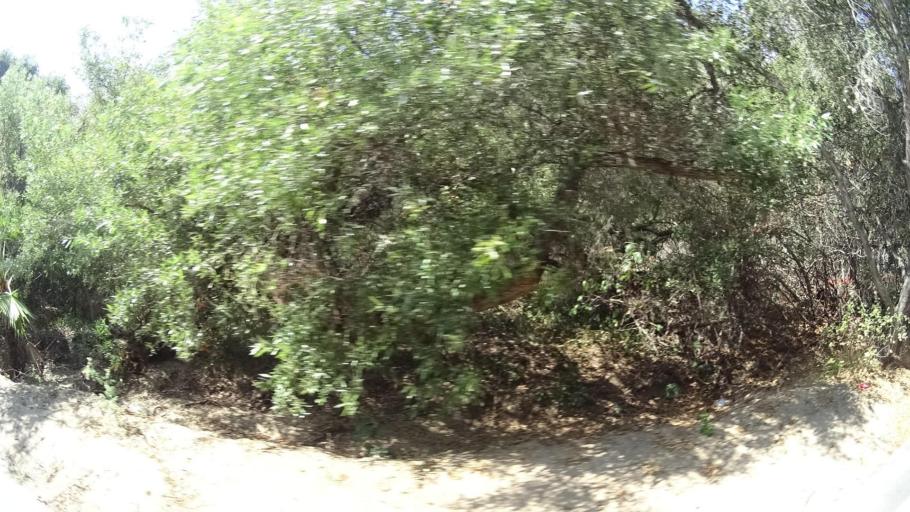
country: US
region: California
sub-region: San Diego County
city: Hidden Meadows
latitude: 33.1855
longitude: -117.1154
